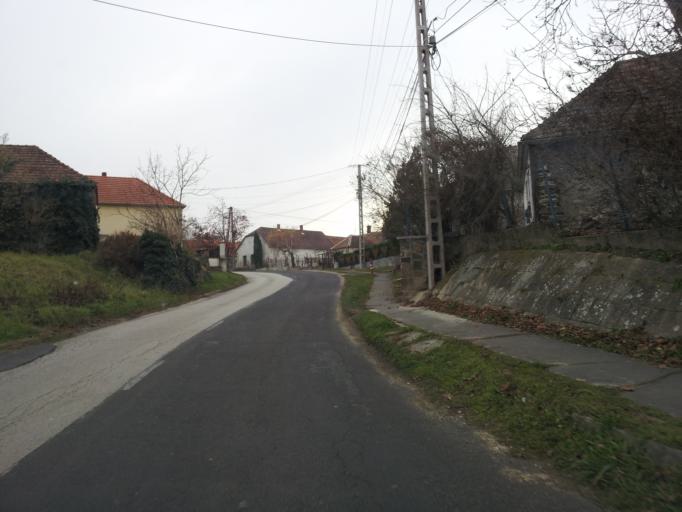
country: HU
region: Veszprem
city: Sumeg
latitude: 46.9333
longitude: 17.2439
